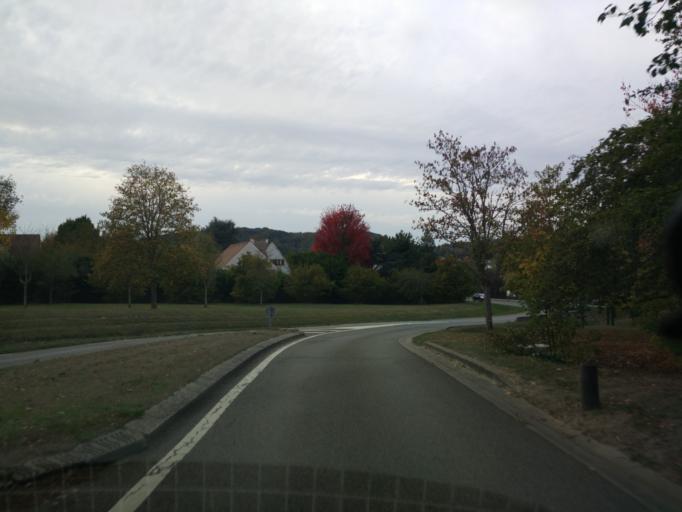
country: FR
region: Ile-de-France
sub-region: Departement des Yvelines
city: Chevreuse
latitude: 48.7034
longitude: 2.0434
